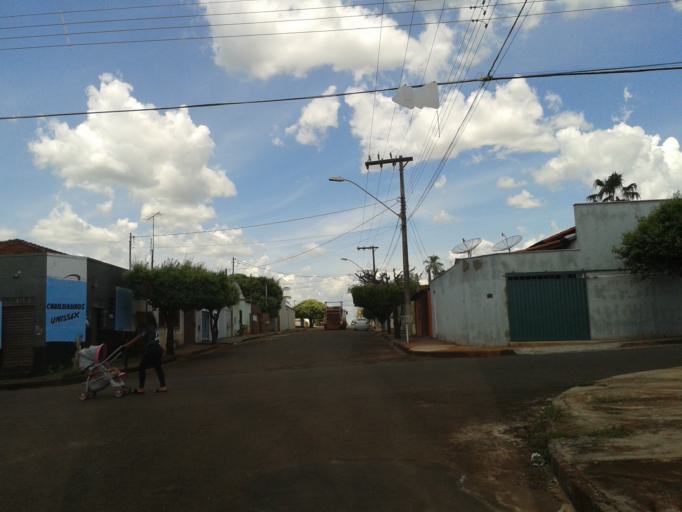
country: BR
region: Minas Gerais
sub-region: Ituiutaba
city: Ituiutaba
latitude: -18.9837
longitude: -49.4712
